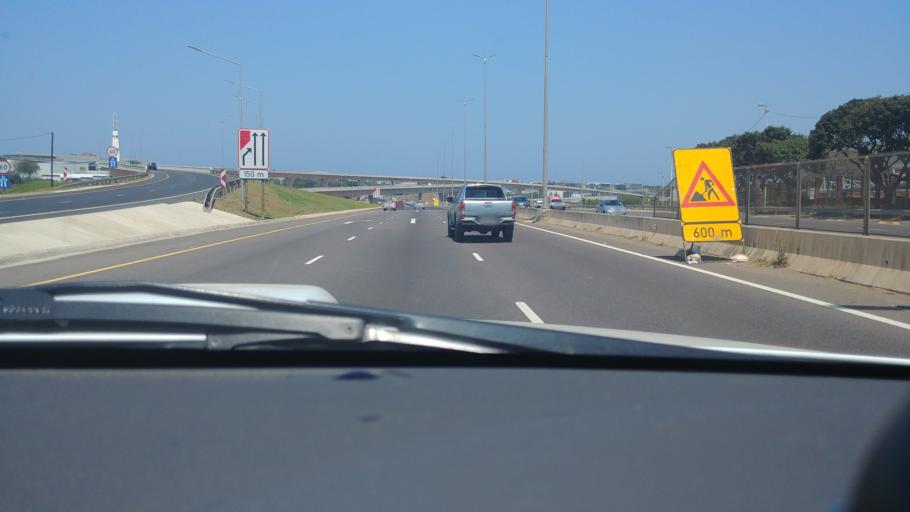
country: ZA
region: KwaZulu-Natal
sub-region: eThekwini Metropolitan Municipality
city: Durban
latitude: -29.7187
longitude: 31.0561
